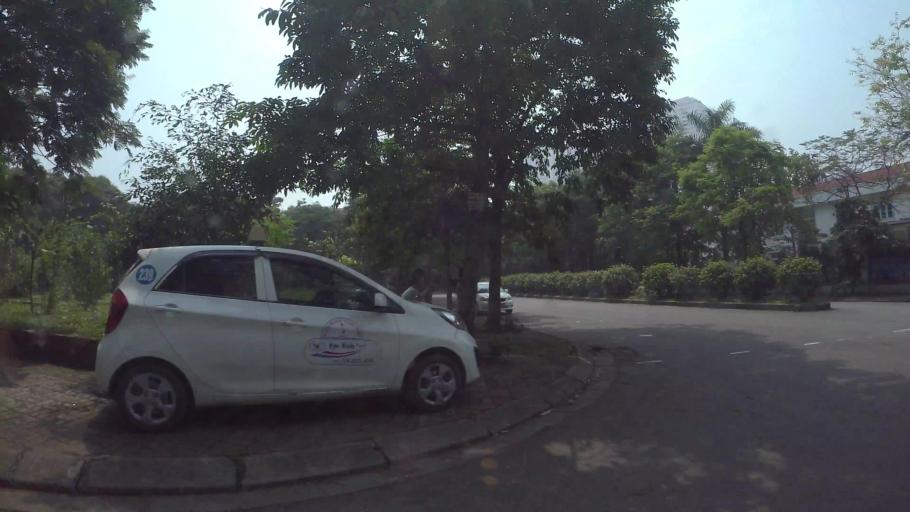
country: VN
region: Ha Noi
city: Van Dien
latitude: 20.9673
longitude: 105.8245
